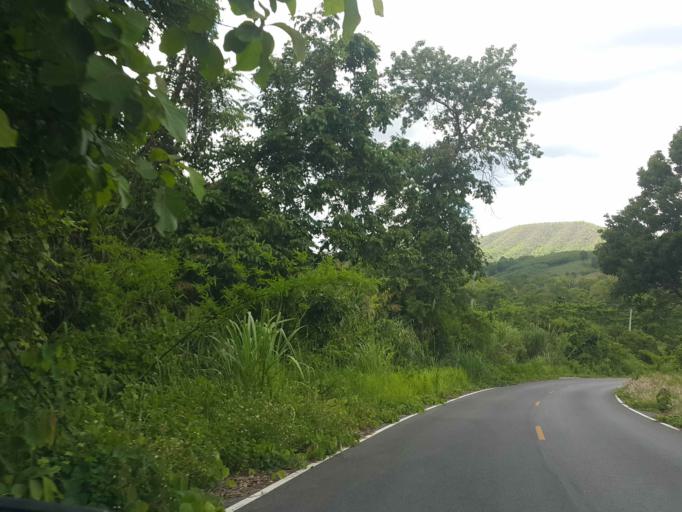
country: TH
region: Nan
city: Wiang Sa
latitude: 18.5349
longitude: 100.5491
